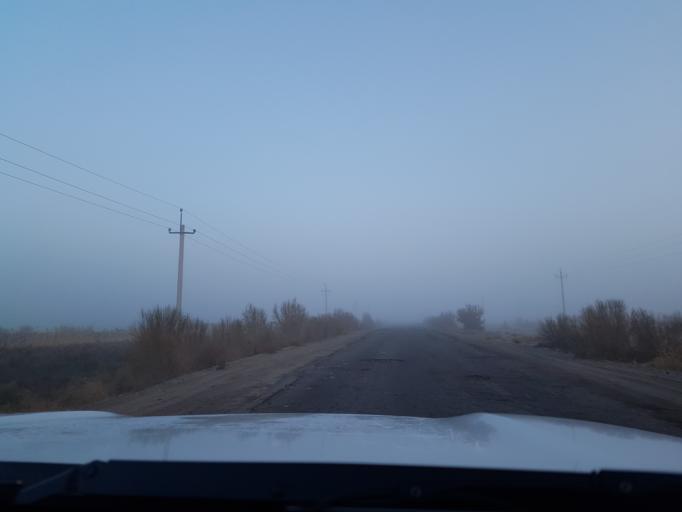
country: TM
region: Dasoguz
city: Koeneuergench
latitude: 41.7983
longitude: 58.7004
